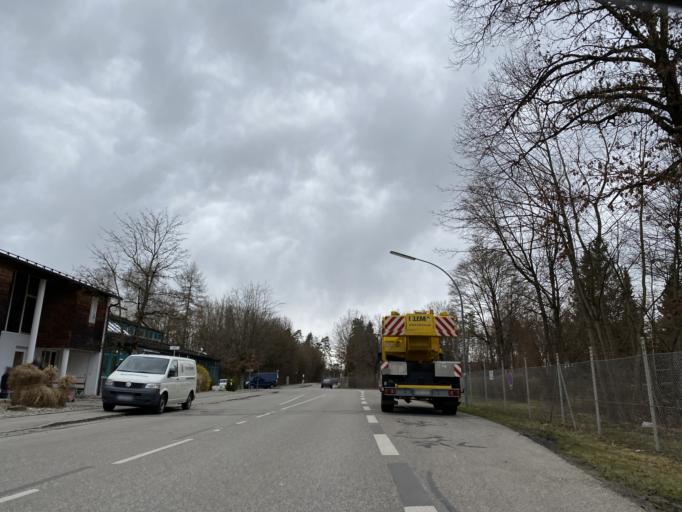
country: DE
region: Bavaria
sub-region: Upper Bavaria
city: Fuerstenfeldbruck
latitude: 48.1912
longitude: 11.2652
